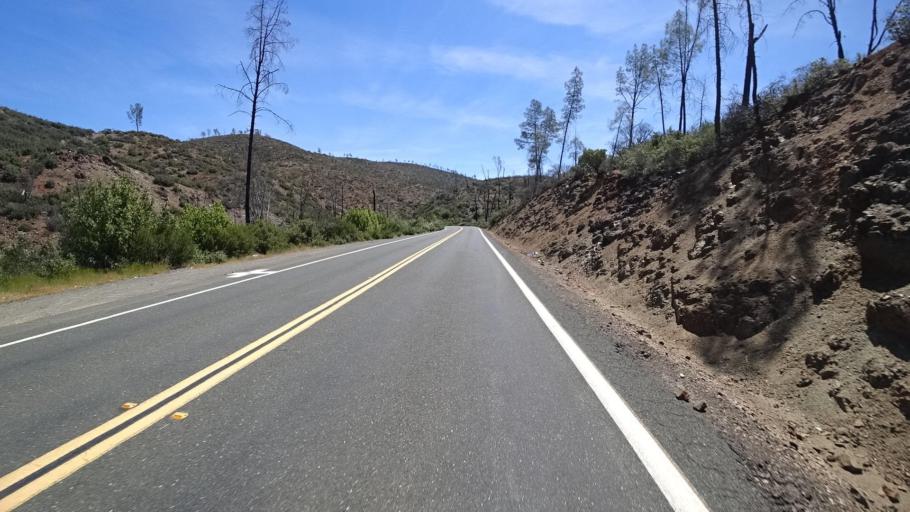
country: US
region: California
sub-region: Lake County
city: Hidden Valley Lake
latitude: 38.7088
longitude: -122.4725
